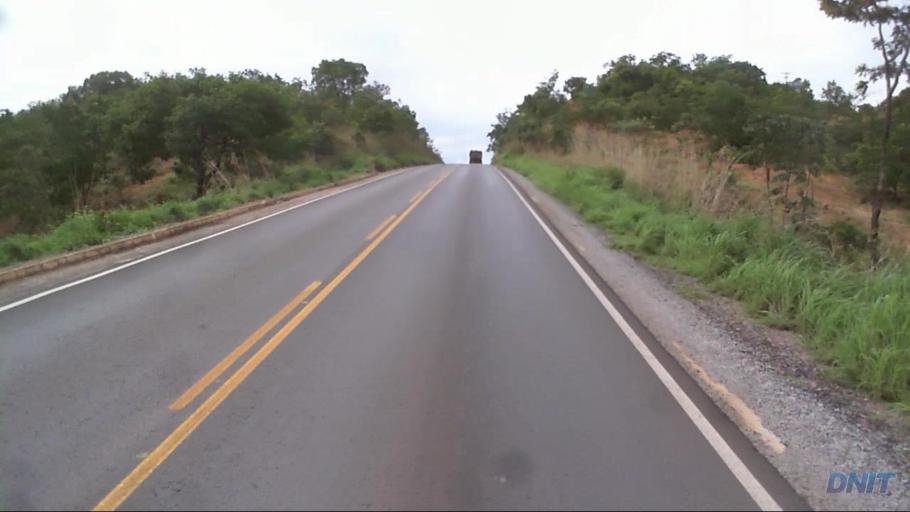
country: BR
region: Goias
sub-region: Padre Bernardo
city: Padre Bernardo
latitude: -15.2163
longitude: -48.2809
